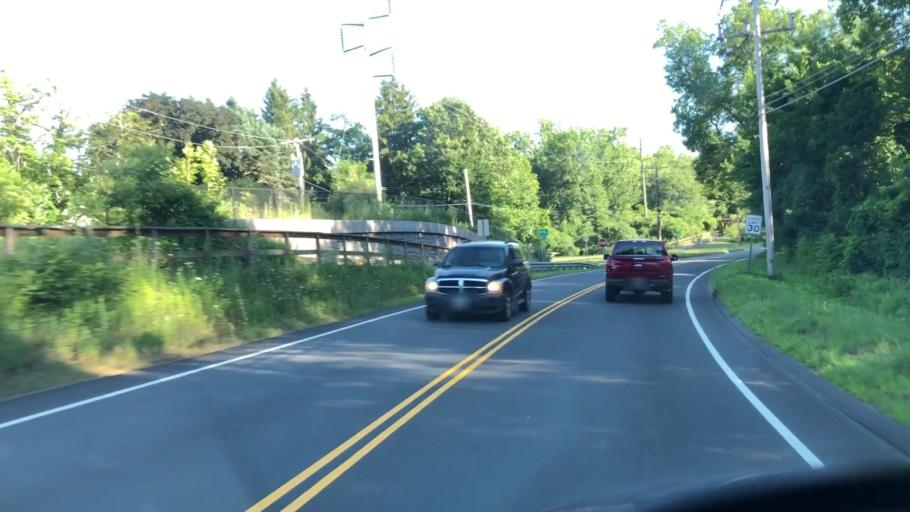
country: US
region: Massachusetts
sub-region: Hampshire County
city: Easthampton
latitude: 42.2816
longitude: -72.6538
